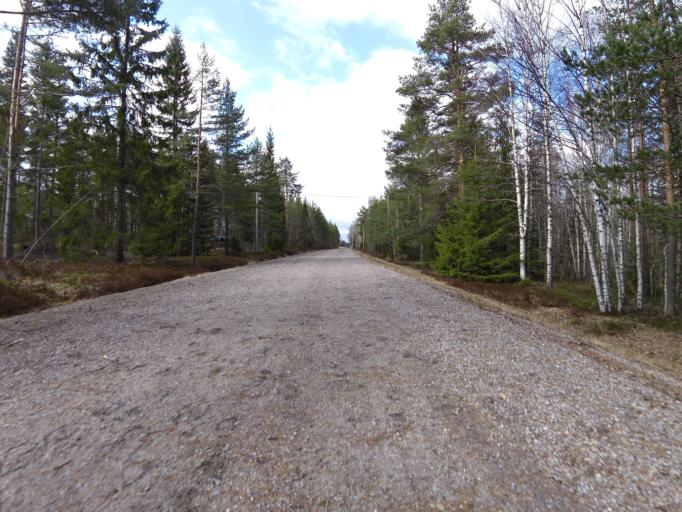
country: SE
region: Gaevleborg
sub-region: Hofors Kommun
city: Hofors
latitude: 60.4818
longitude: 16.4469
